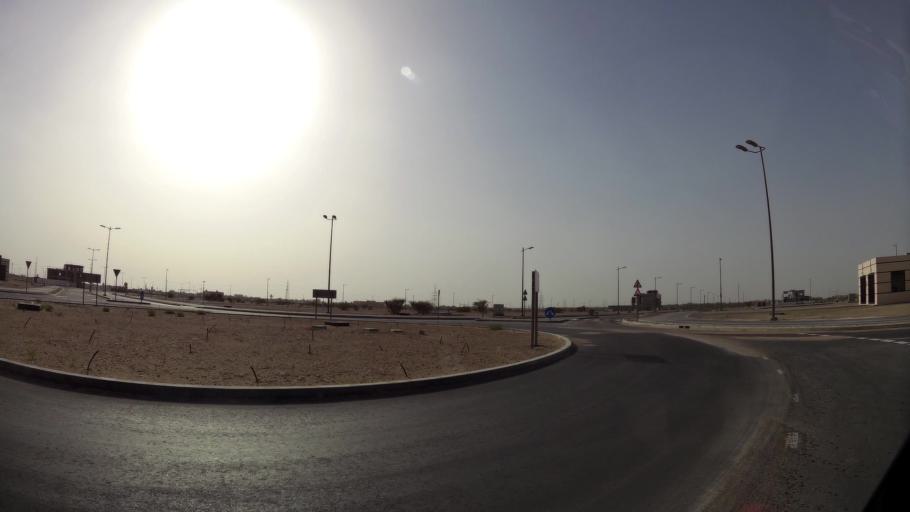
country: AE
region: Abu Dhabi
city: Al Ain
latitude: 24.1237
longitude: 55.7227
